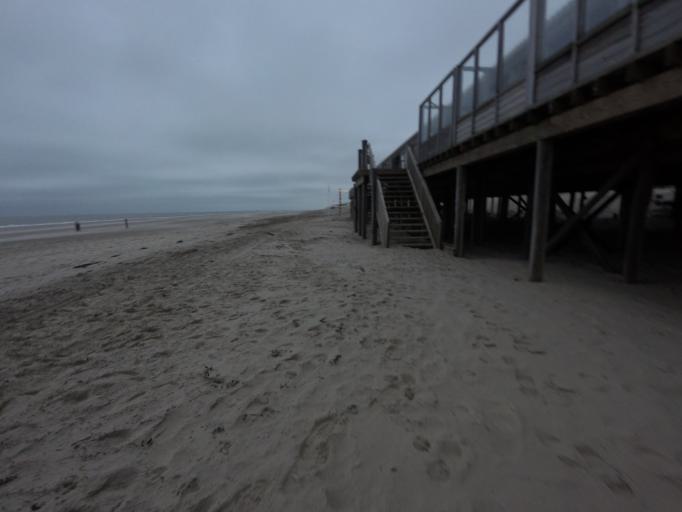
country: NL
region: North Holland
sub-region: Gemeente Texel
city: Den Burg
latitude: 53.0962
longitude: 4.7492
